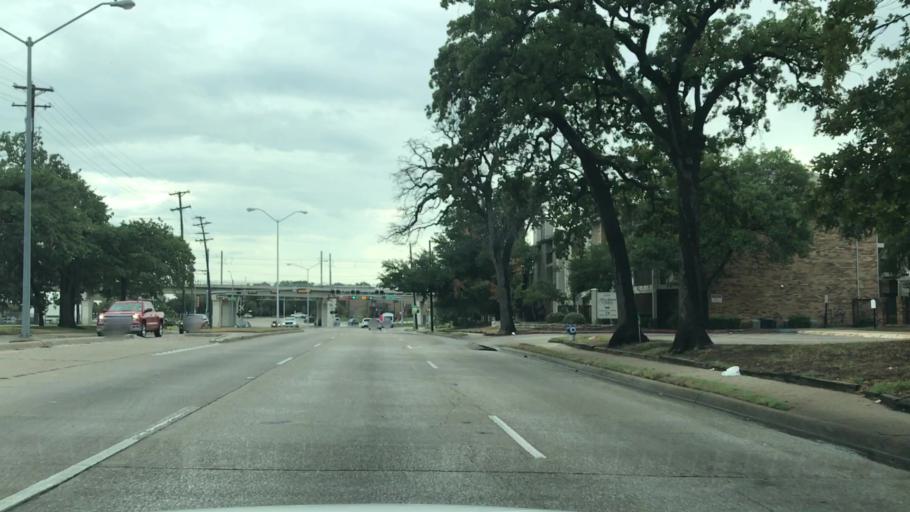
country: US
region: Texas
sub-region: Dallas County
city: University Park
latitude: 32.8532
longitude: -96.8752
